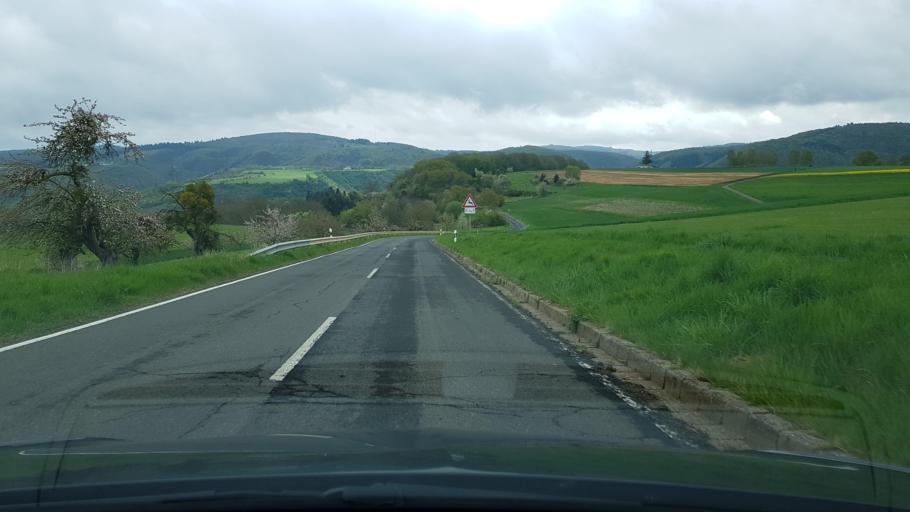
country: DE
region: Rheinland-Pfalz
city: Lof
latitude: 50.2484
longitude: 7.4253
